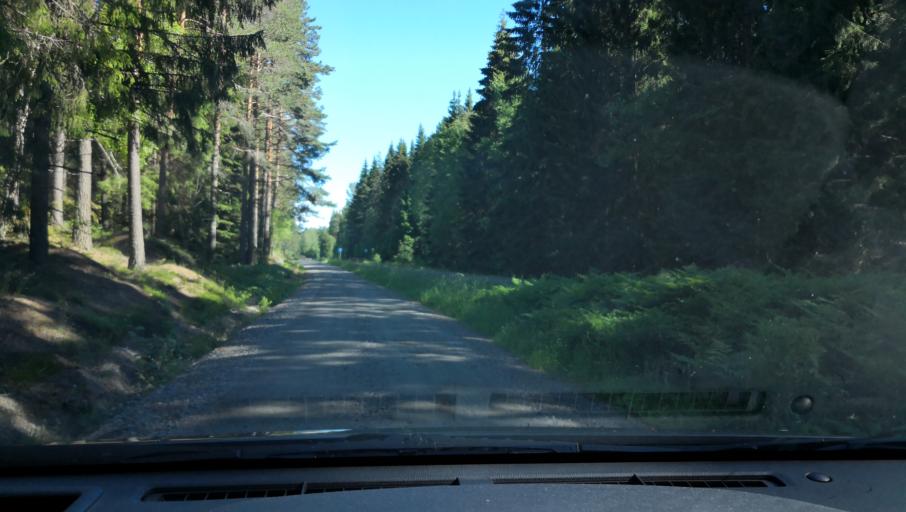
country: SE
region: Soedermanland
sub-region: Eskilstuna Kommun
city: Eskilstuna
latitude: 59.3341
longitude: 16.5755
